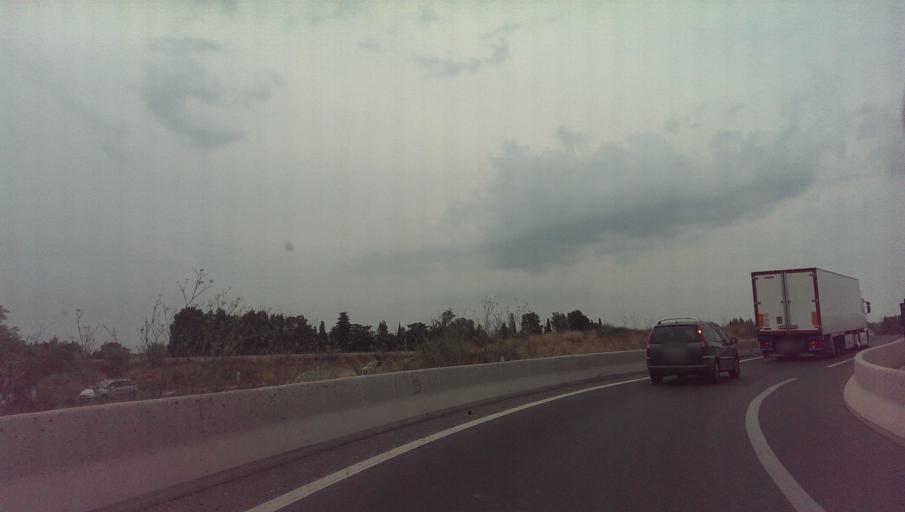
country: FR
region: Languedoc-Roussillon
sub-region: Departement des Pyrenees-Orientales
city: Saint-Esteve
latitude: 42.7005
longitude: 2.8653
